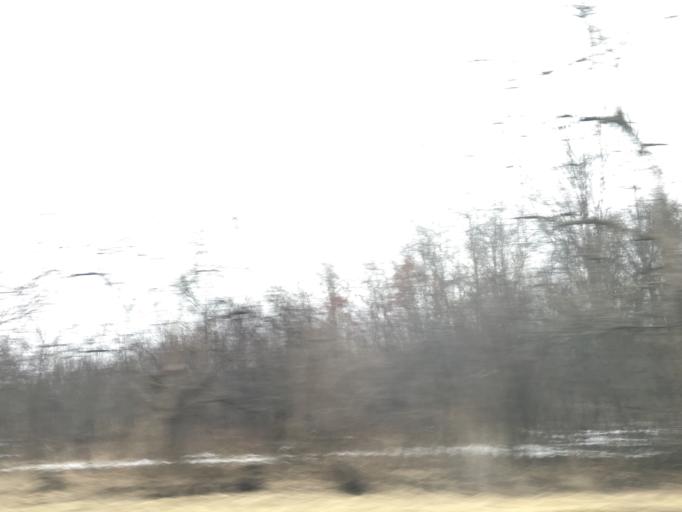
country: US
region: Illinois
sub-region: Cook County
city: Streamwood
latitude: 42.0610
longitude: -88.1598
